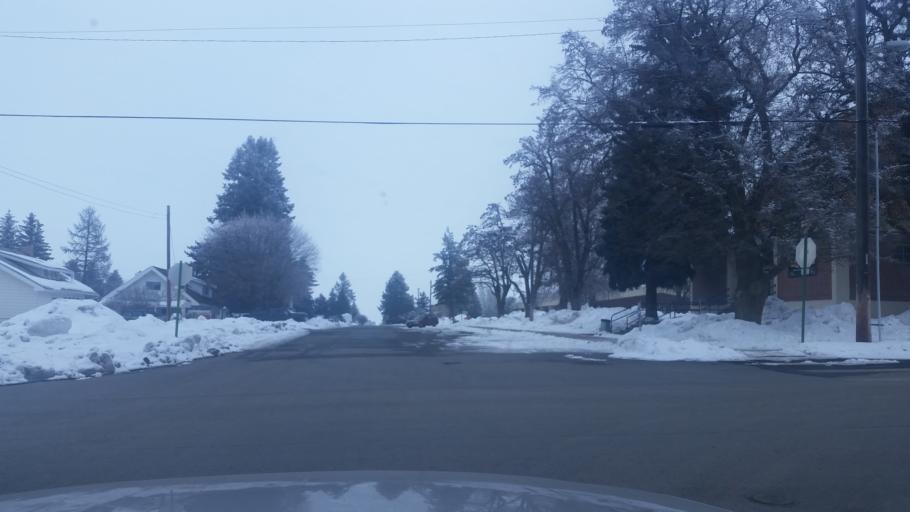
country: US
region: Washington
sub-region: Spokane County
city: Medical Lake
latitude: 47.6684
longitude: -117.8781
